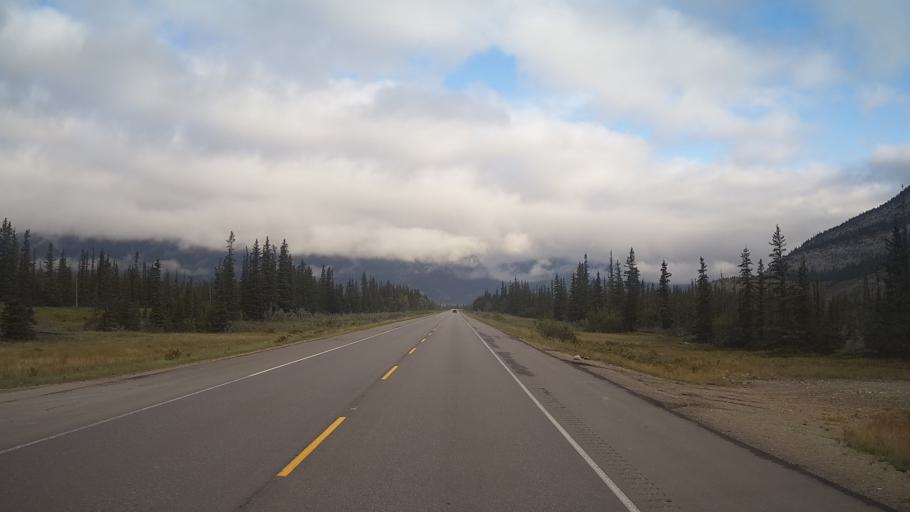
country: CA
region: Alberta
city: Jasper Park Lodge
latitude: 53.0181
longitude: -118.0809
